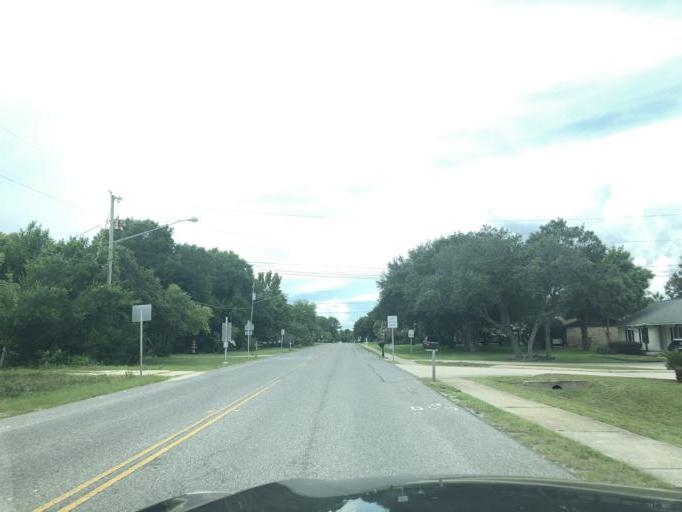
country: US
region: Florida
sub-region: Okaloosa County
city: Destin
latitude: 30.4025
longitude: -86.4952
